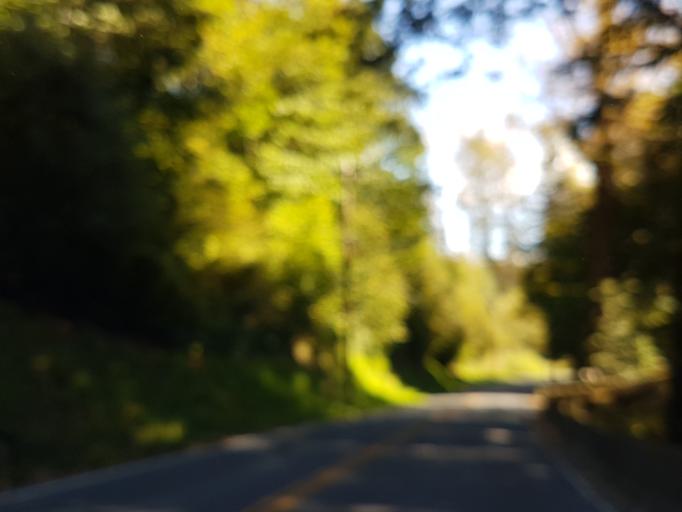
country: US
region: Washington
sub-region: Snohomish County
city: Cathcart
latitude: 47.8444
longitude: -122.0965
